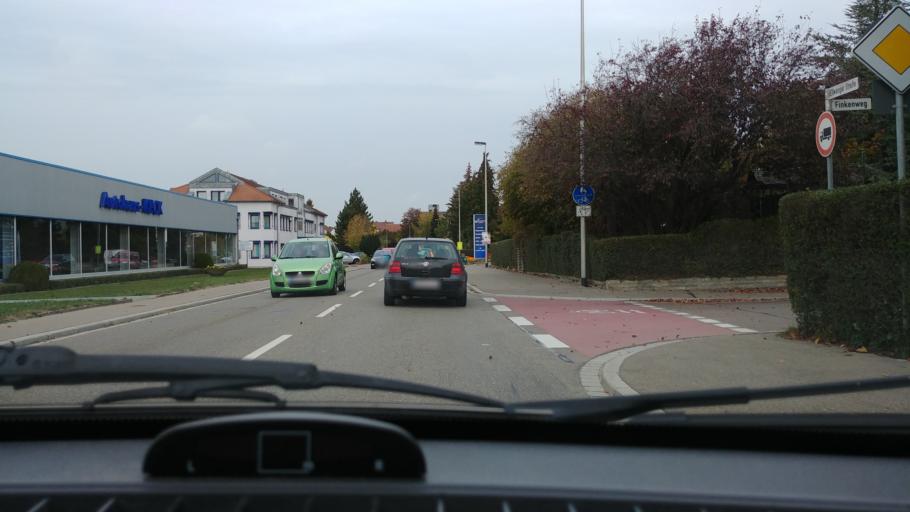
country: DE
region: Baden-Wuerttemberg
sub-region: Regierungsbezirk Stuttgart
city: Crailsheim
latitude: 49.1290
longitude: 10.0786
